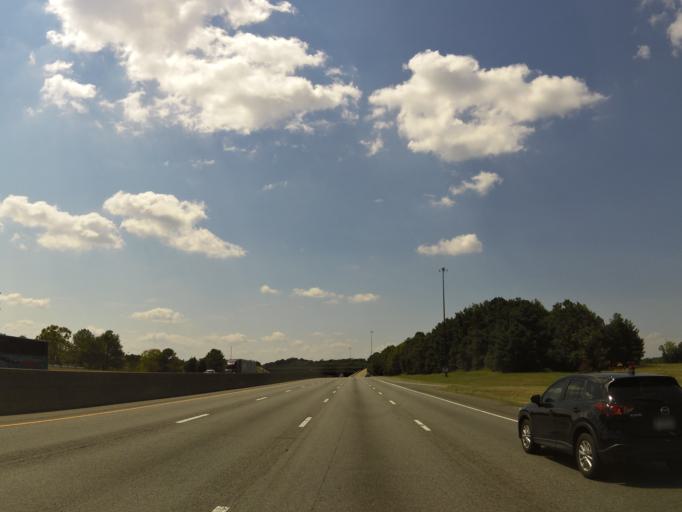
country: US
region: North Carolina
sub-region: Mecklenburg County
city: Charlotte
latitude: 35.2731
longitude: -80.8399
